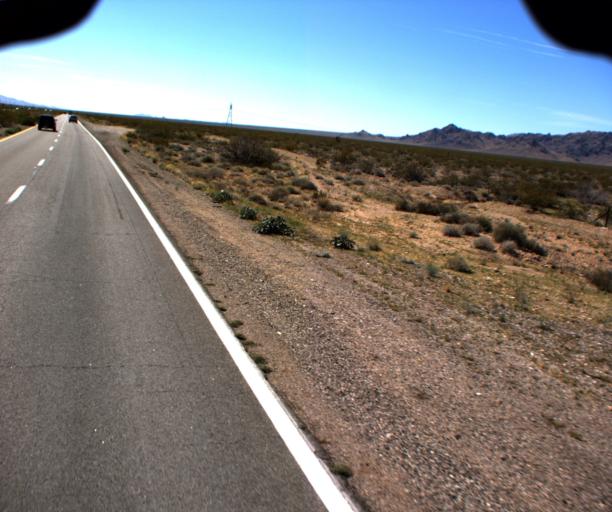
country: US
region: Arizona
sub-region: Mohave County
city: Dolan Springs
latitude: 35.6786
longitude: -114.4654
